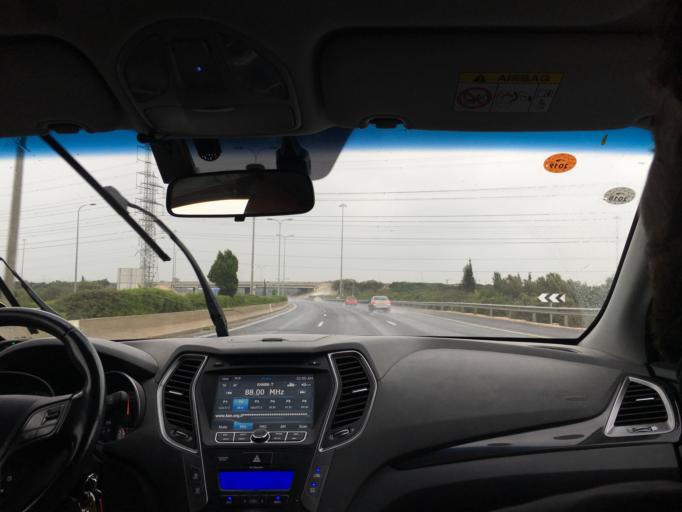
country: IL
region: Central District
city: Petah Tiqwa
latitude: 32.1178
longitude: 34.8754
